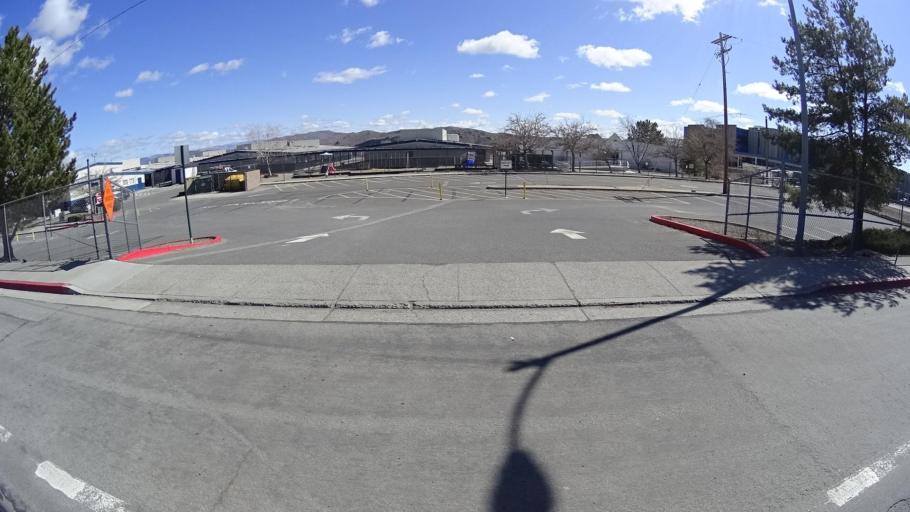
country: US
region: Nevada
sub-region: Washoe County
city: Lemmon Valley
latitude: 39.6235
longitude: -119.8821
